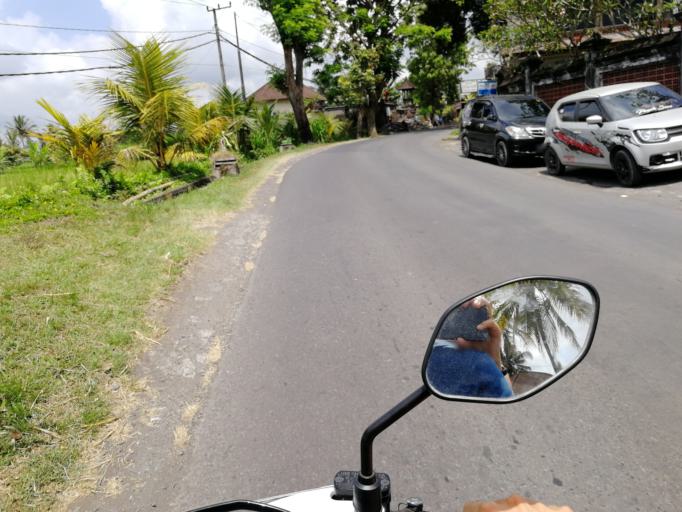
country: ID
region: Bali
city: Banjar Geriana Kangin
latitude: -8.4374
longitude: 115.4787
